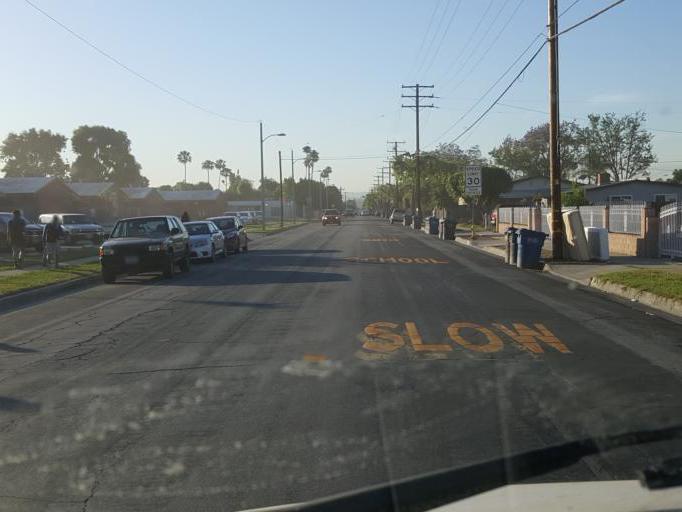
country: US
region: California
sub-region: Los Angeles County
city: West Puente Valley
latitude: 34.0559
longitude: -117.9682
